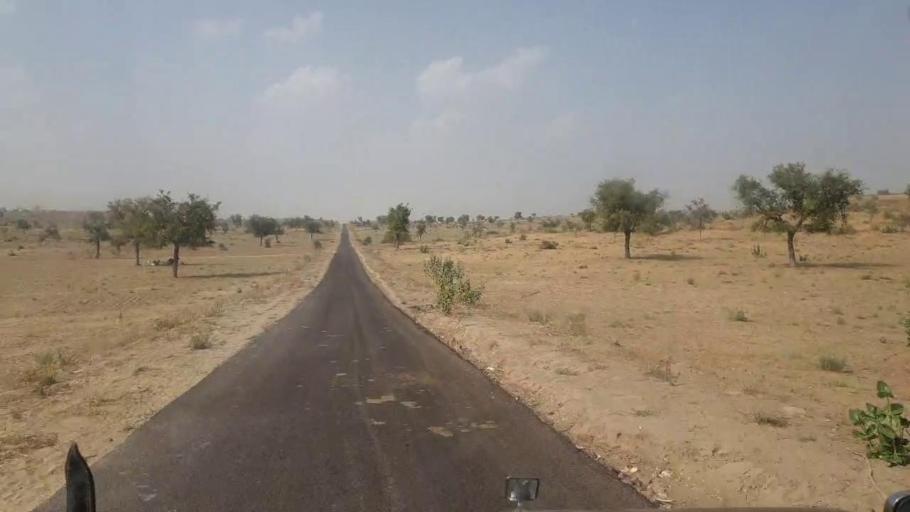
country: PK
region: Sindh
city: Islamkot
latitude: 25.1864
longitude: 70.2862
